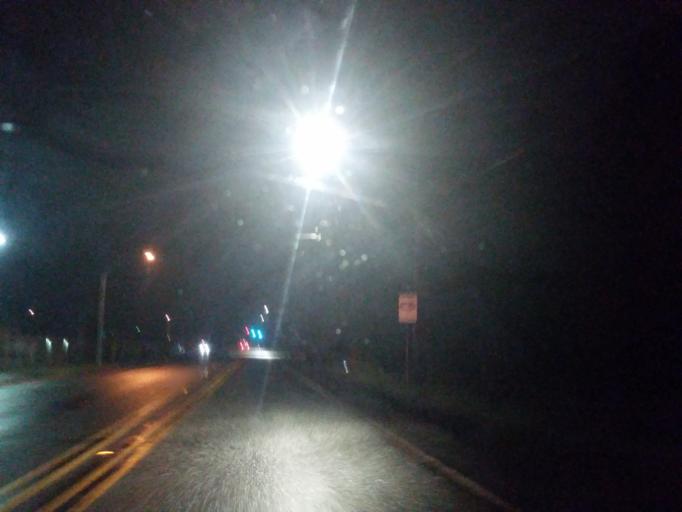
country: US
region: Washington
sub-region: King County
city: Pacific
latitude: 47.2381
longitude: -122.2544
